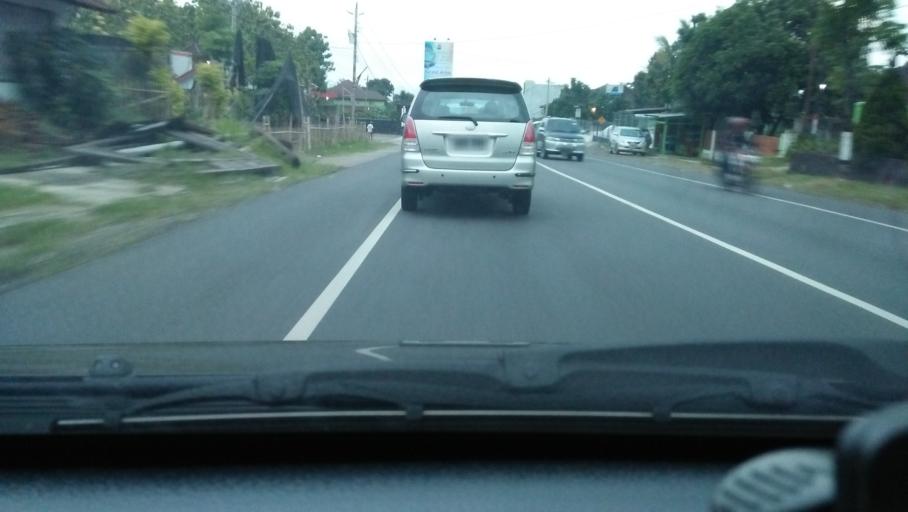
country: ID
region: Central Java
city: Magelang
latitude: -7.4098
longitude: 110.2374
